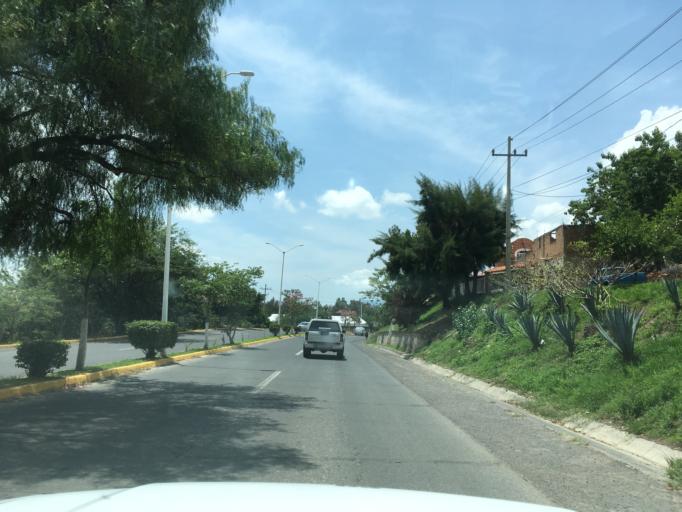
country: MX
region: Jalisco
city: Tlajomulco de Zuniga
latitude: 20.4677
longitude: -103.4512
